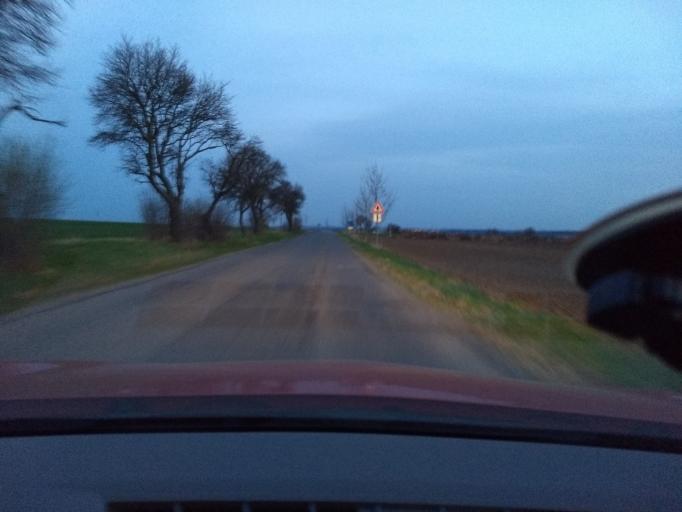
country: CZ
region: Central Bohemia
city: Jenec
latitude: 50.0546
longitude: 14.1890
